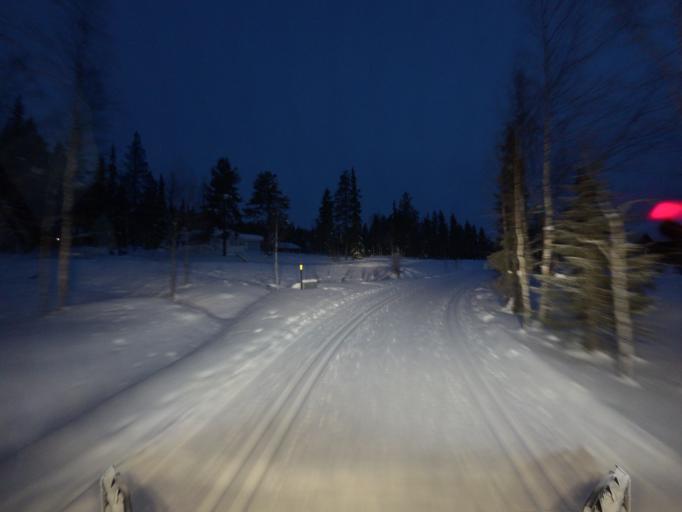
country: FI
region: Lapland
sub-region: Tunturi-Lappi
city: Kolari
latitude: 67.6054
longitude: 24.1361
